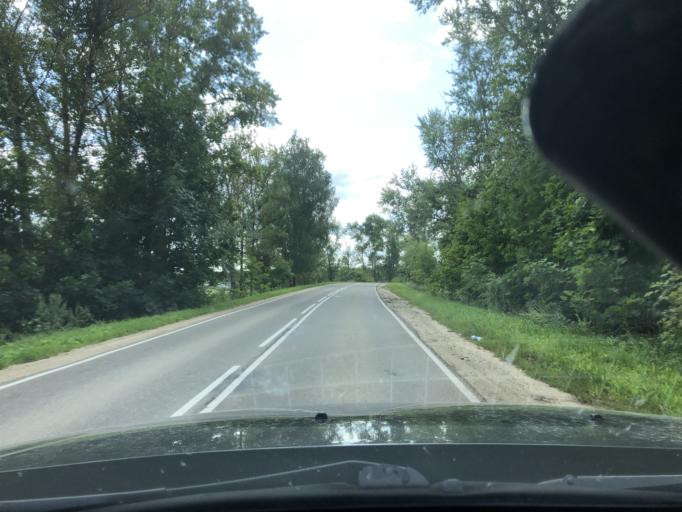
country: RU
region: Tula
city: Revyakino
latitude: 54.3556
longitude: 37.6347
